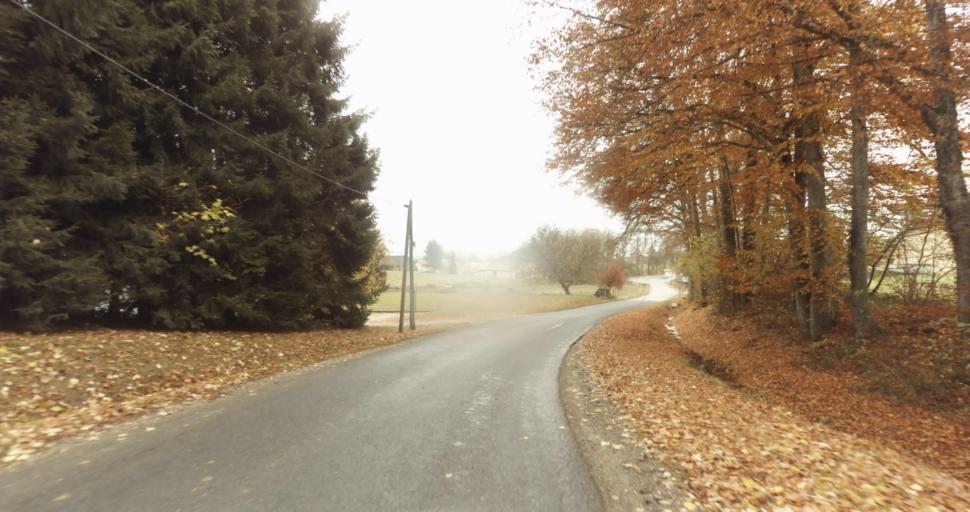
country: FR
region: Rhone-Alpes
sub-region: Departement de la Haute-Savoie
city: Evires
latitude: 46.0553
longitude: 6.2094
